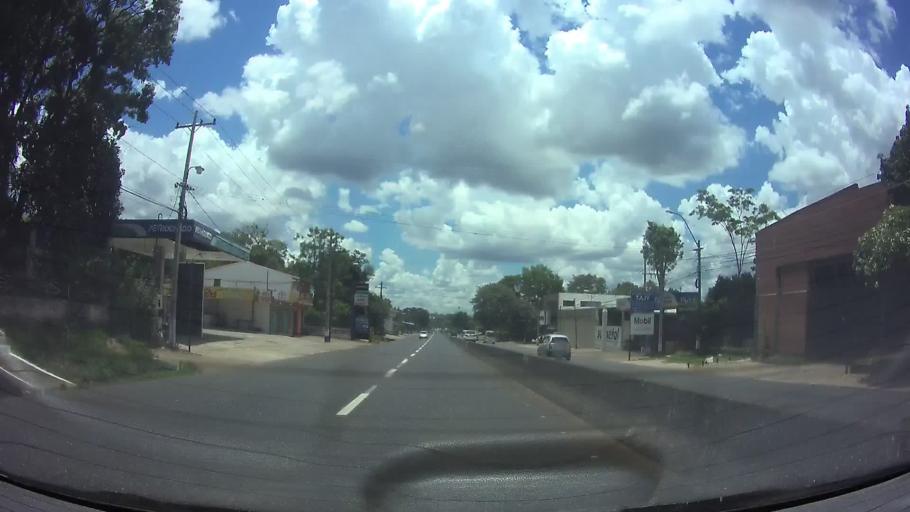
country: PY
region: Central
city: Capiata
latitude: -25.3656
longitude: -57.4235
